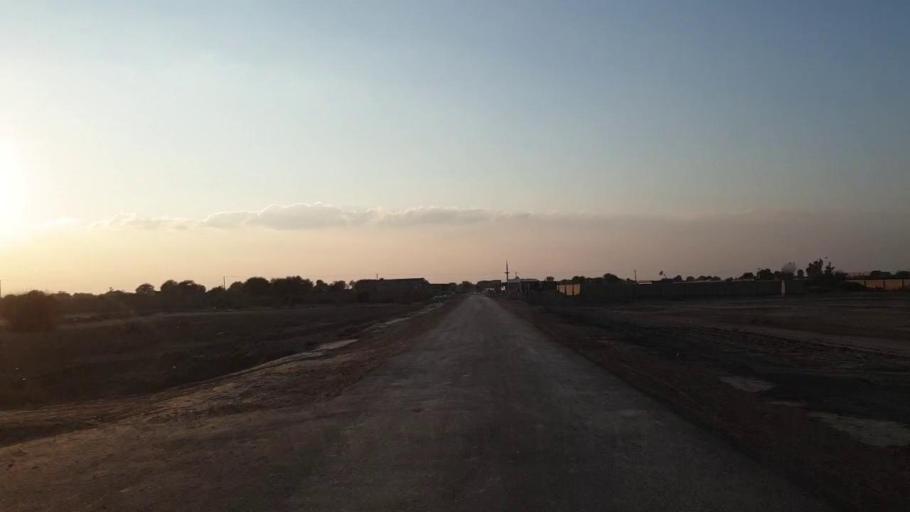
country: PK
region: Sindh
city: Shahpur Chakar
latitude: 26.1577
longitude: 68.5457
